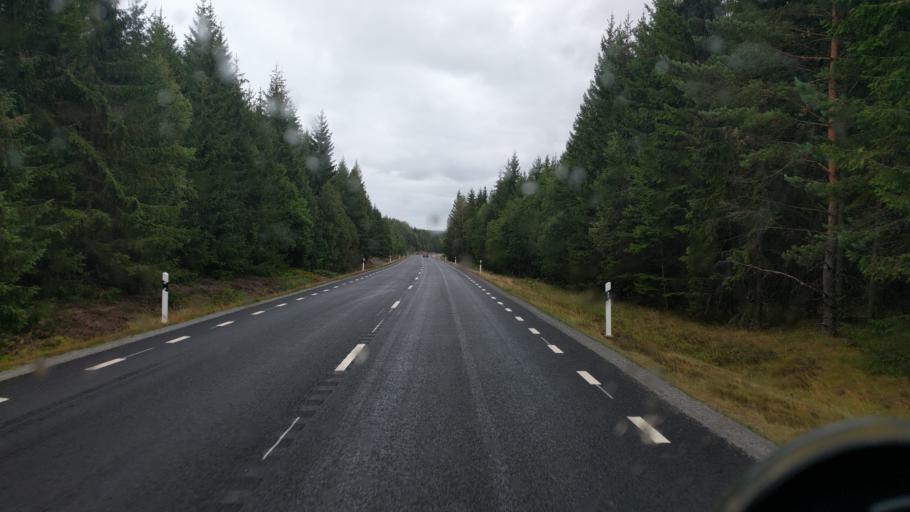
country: SE
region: Kalmar
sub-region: Vasterviks Kommun
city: Ankarsrum
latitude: 57.7233
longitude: 16.3808
